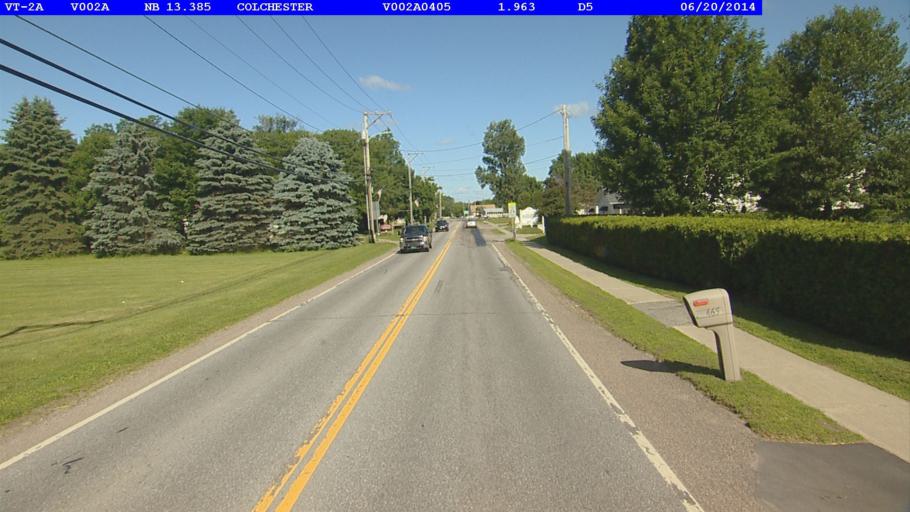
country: US
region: Vermont
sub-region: Chittenden County
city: Colchester
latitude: 44.5472
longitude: -73.1568
